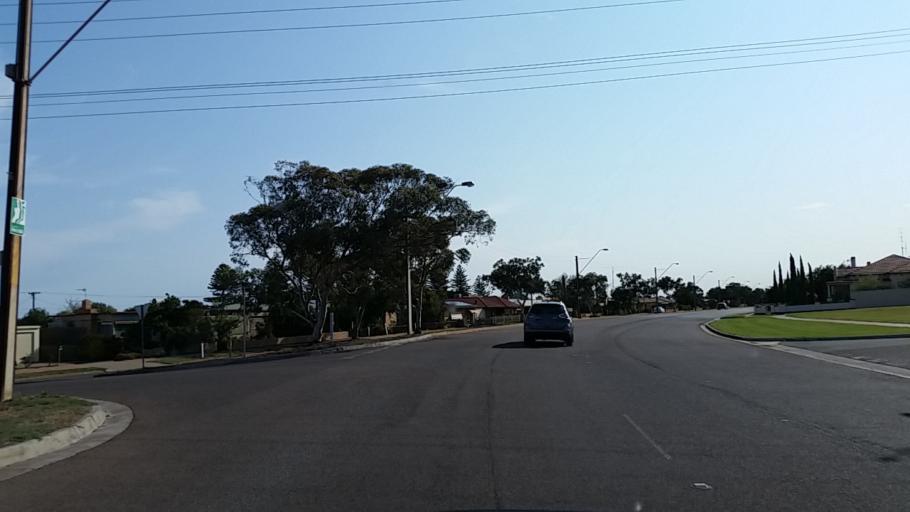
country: AU
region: South Australia
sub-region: Whyalla
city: Whyalla
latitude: -33.0413
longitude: 137.5767
